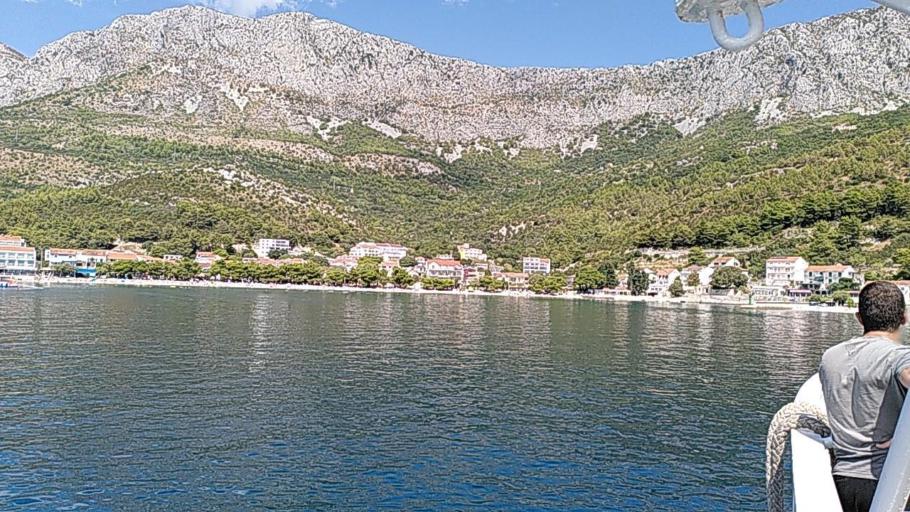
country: HR
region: Splitsko-Dalmatinska
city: Vrgorac
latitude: 43.1525
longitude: 17.2466
